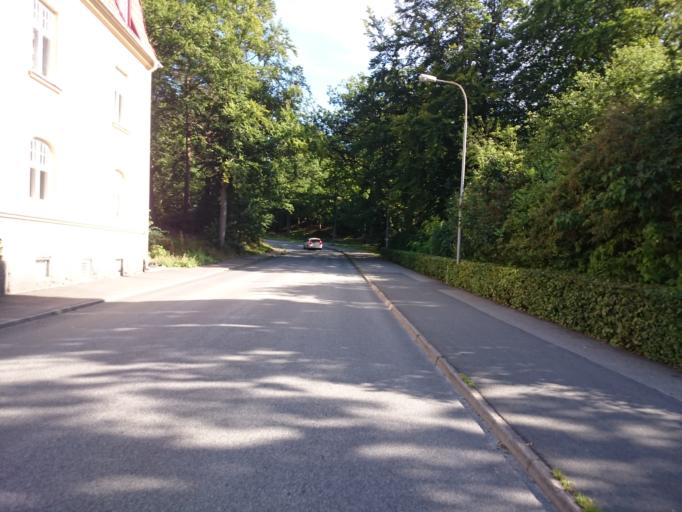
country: SE
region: Blekinge
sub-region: Karlshamns Kommun
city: Karlshamn
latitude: 56.1665
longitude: 14.8732
